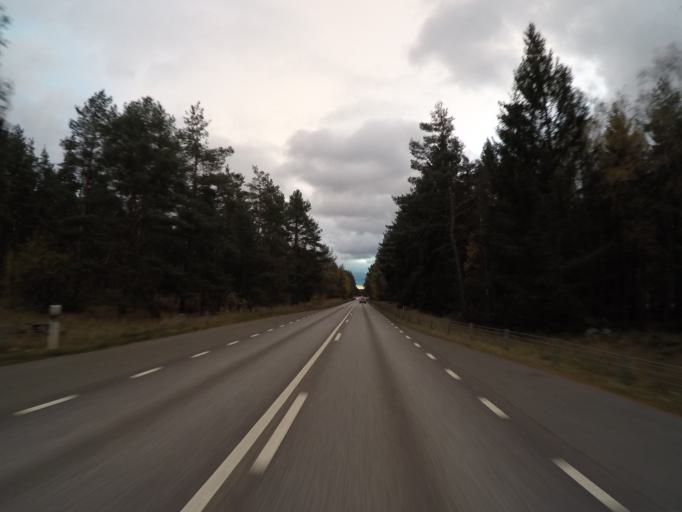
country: SE
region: Skane
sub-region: Kristianstads Kommun
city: Degeberga
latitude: 55.9151
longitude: 14.0727
